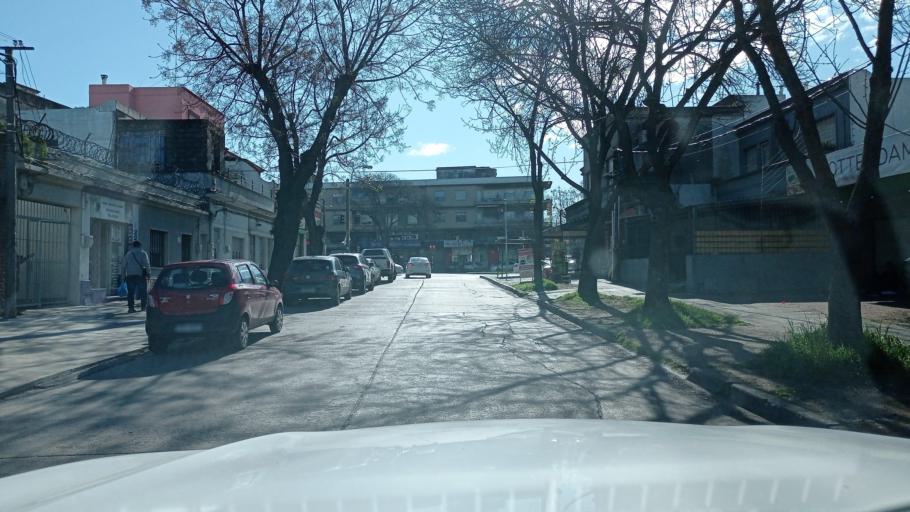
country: UY
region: Montevideo
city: Montevideo
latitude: -34.8536
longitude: -56.1603
